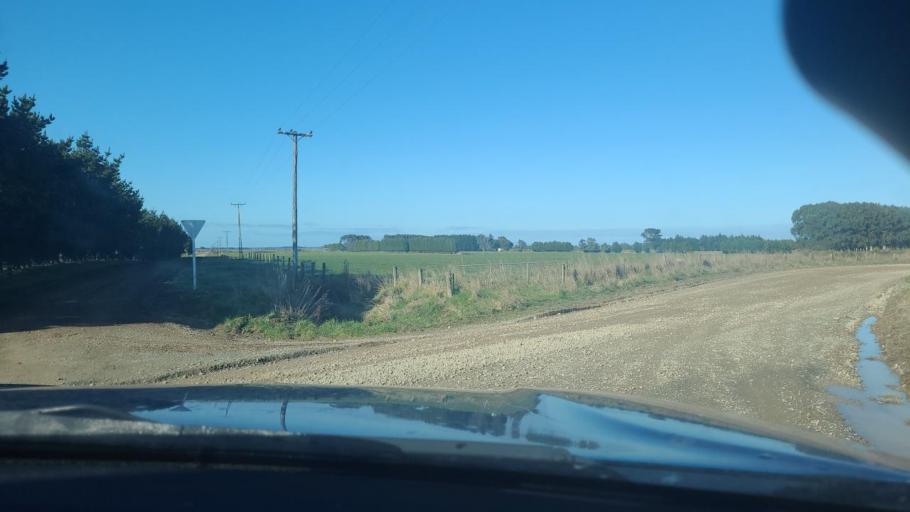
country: NZ
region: Southland
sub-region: Invercargill City
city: Invercargill
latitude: -46.3306
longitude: 168.2279
